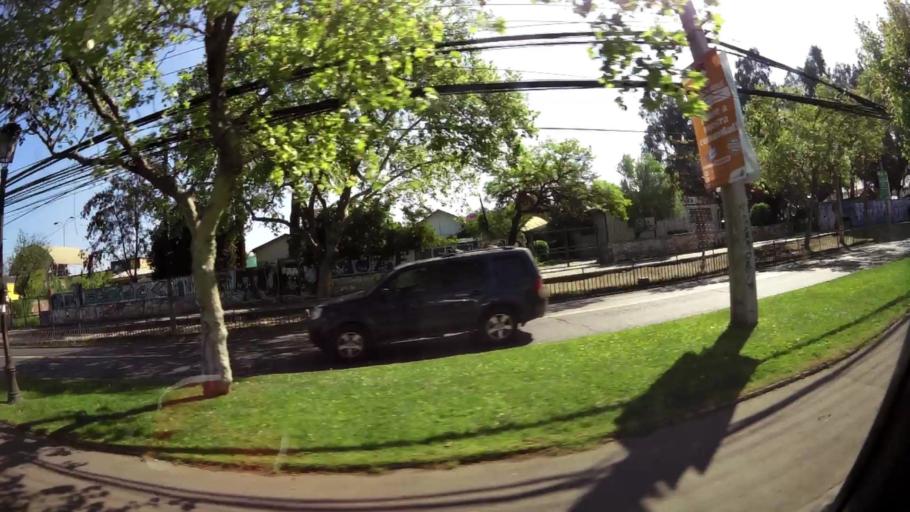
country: CL
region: Santiago Metropolitan
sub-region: Provincia de Santiago
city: Lo Prado
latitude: -33.5046
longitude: -70.7574
